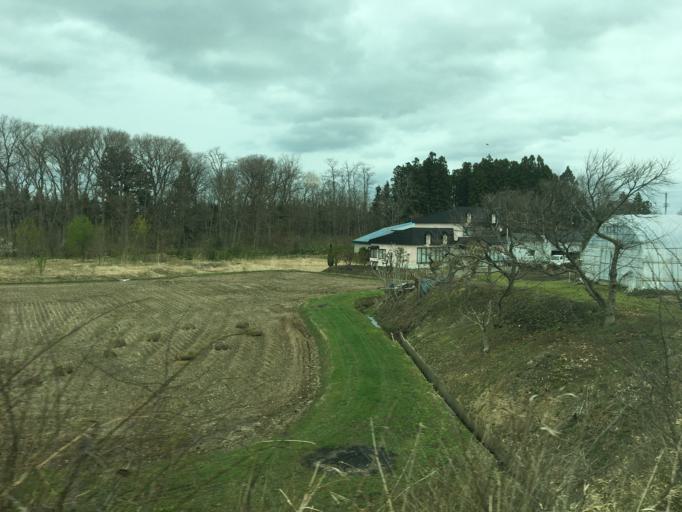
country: JP
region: Aomori
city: Shimokizukuri
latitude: 40.7871
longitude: 140.2954
